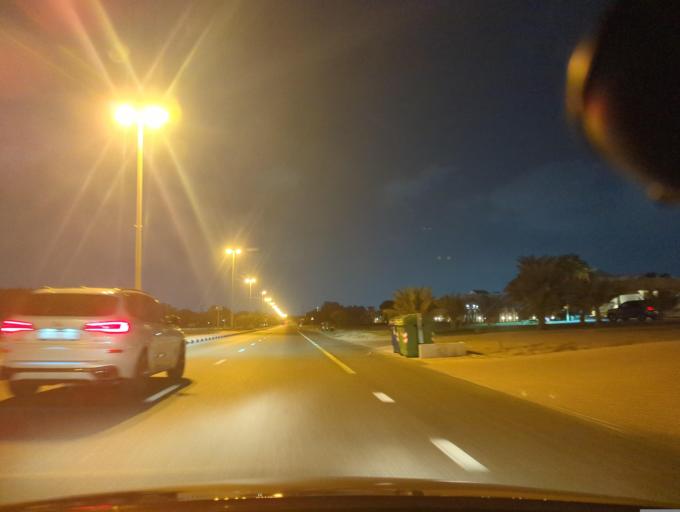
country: AE
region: Ash Shariqah
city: Sharjah
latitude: 25.3502
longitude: 55.4638
